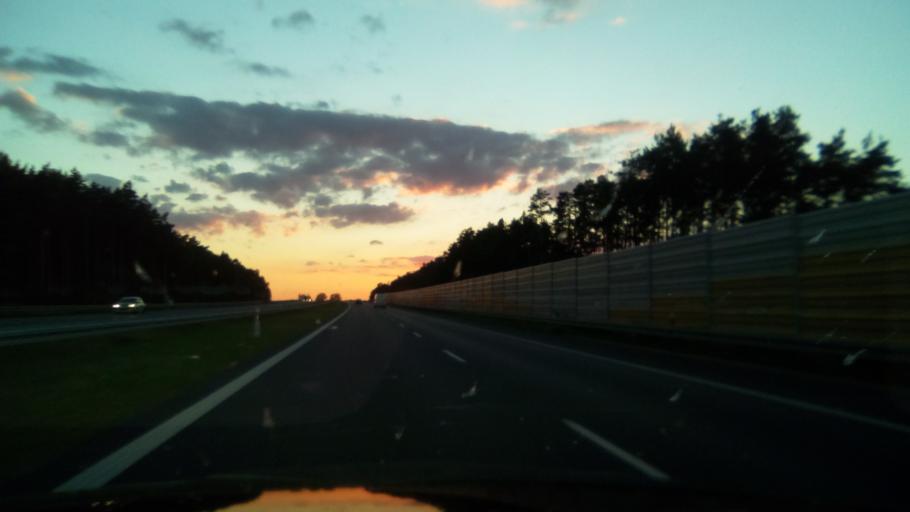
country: PL
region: Lodz Voivodeship
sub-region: Powiat leczycki
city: Swinice Warckie
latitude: 52.0242
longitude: 18.9226
